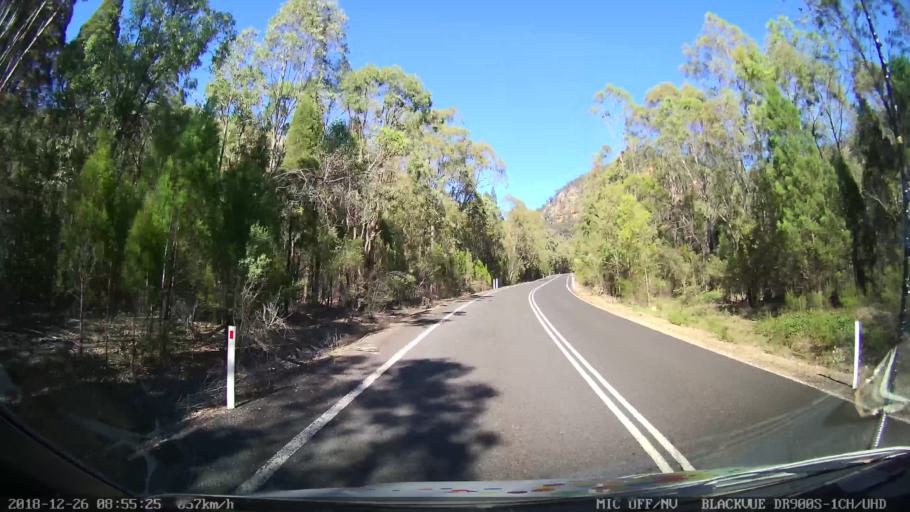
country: AU
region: New South Wales
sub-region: Mid-Western Regional
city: Kandos
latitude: -32.6210
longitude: 150.0656
